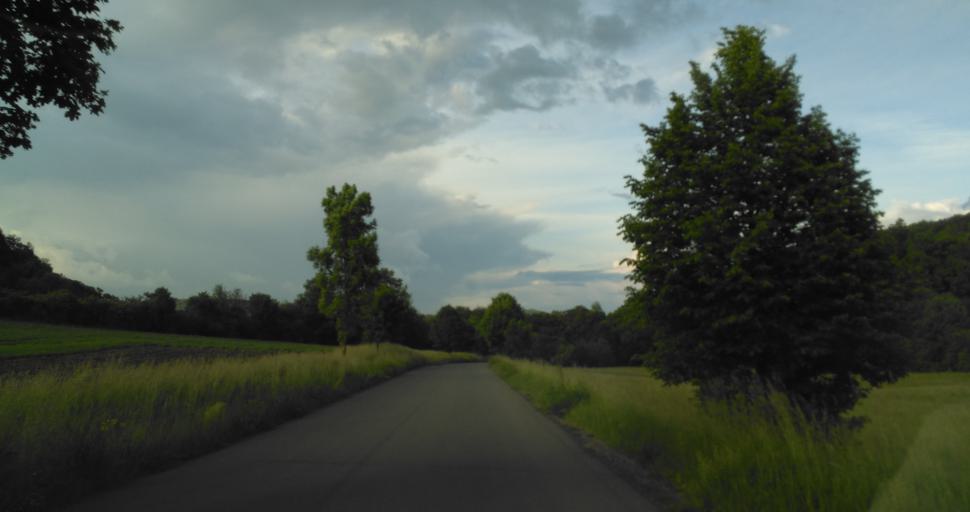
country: CZ
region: Central Bohemia
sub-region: Okres Beroun
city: Beroun
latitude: 49.9417
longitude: 14.0906
